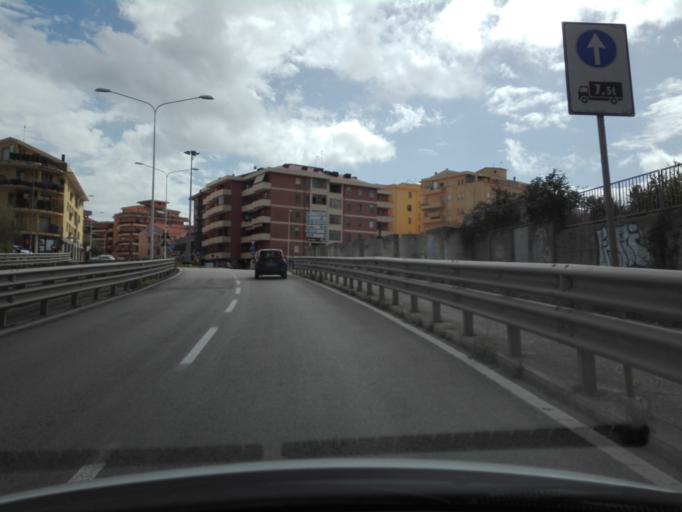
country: IT
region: Sardinia
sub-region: Provincia di Sassari
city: Sassari
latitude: 40.7293
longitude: 8.5757
